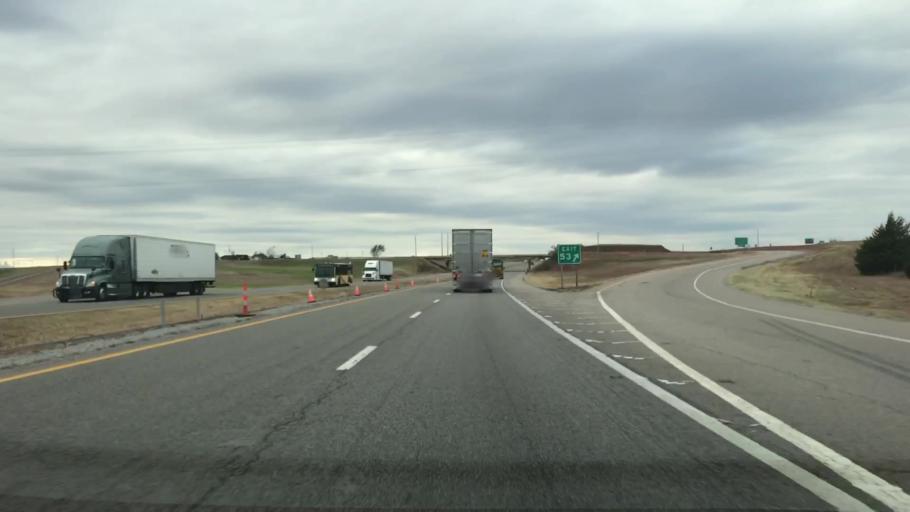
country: US
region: Oklahoma
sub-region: Washita County
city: Burns Flat
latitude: 35.4453
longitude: -99.1677
